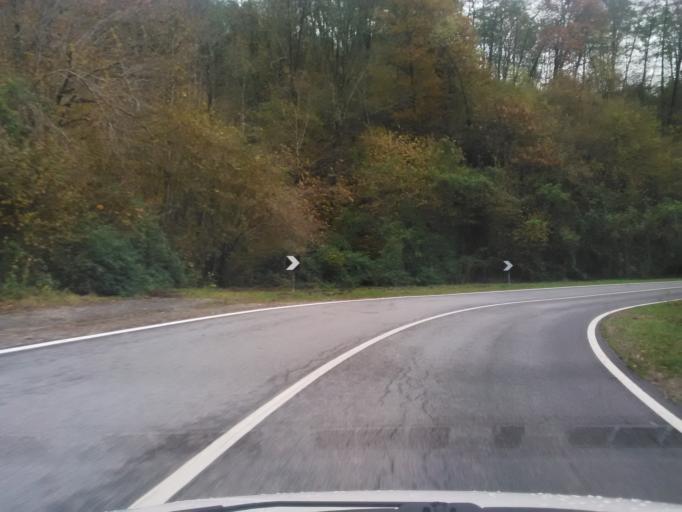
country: IT
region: Piedmont
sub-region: Provincia di Vercelli
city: Valduggia
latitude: 45.7384
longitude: 8.3475
